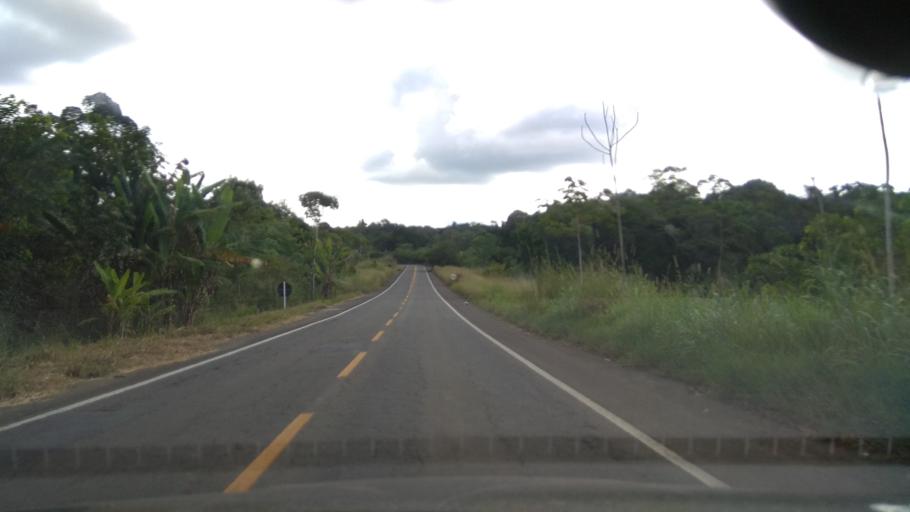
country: BR
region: Bahia
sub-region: Ubaitaba
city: Ubaitaba
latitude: -14.2640
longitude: -39.3309
